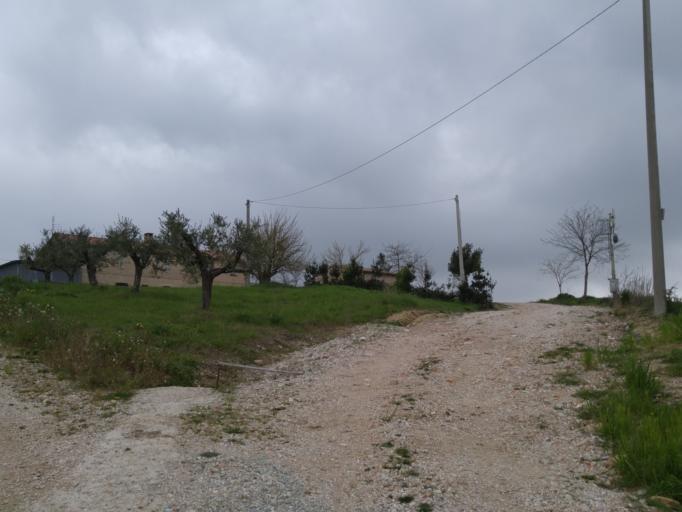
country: IT
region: The Marches
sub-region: Provincia di Pesaro e Urbino
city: Calcinelli
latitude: 43.7627
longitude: 12.9105
